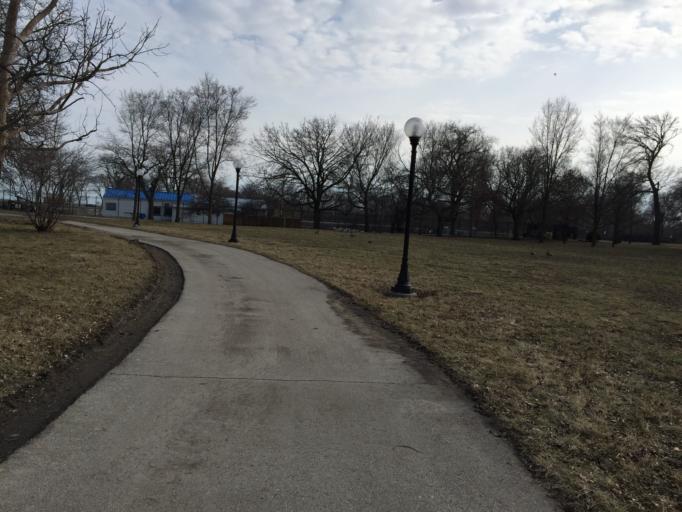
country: US
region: Illinois
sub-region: Cook County
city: Chicago
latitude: 41.7891
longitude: -87.5802
